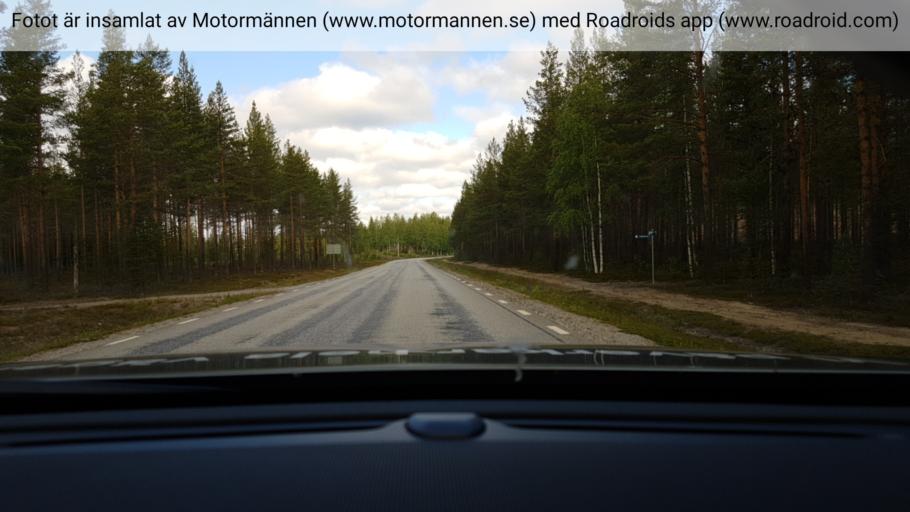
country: SE
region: Vaesterbotten
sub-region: Lycksele Kommun
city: Lycksele
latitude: 64.8294
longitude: 18.7876
